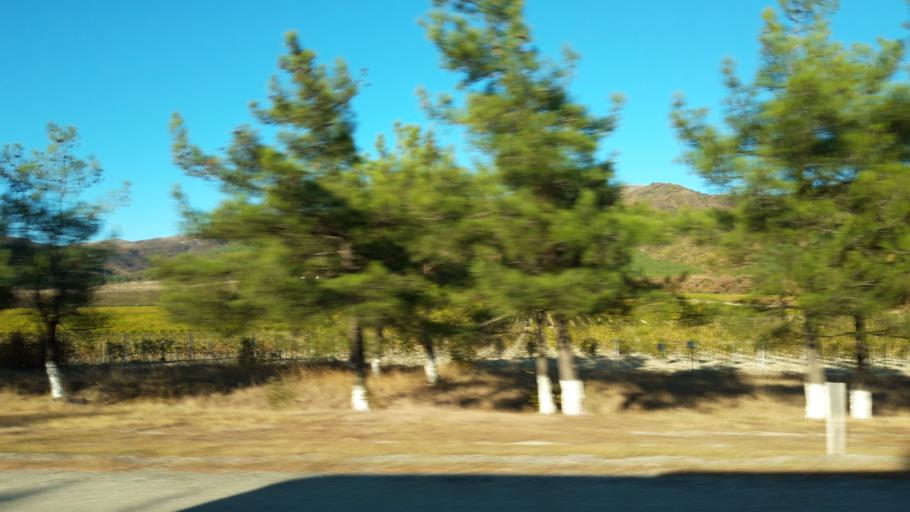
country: RU
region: Krasnodarskiy
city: Kabardinka
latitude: 44.6245
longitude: 38.0134
